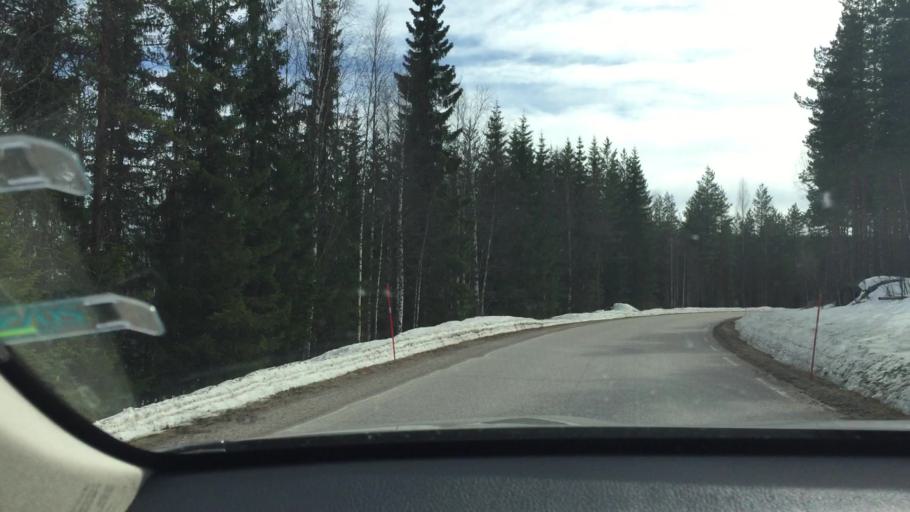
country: NO
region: Hedmark
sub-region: Trysil
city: Innbygda
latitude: 61.0690
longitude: 12.5565
